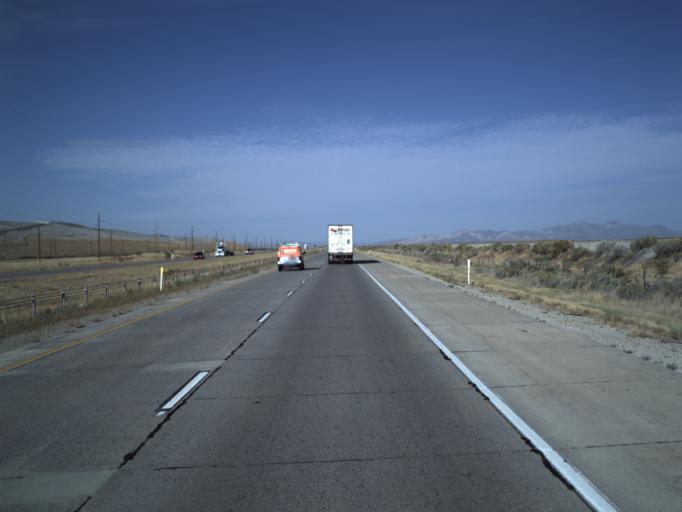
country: US
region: Utah
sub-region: Salt Lake County
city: Magna
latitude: 40.7710
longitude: -112.1149
